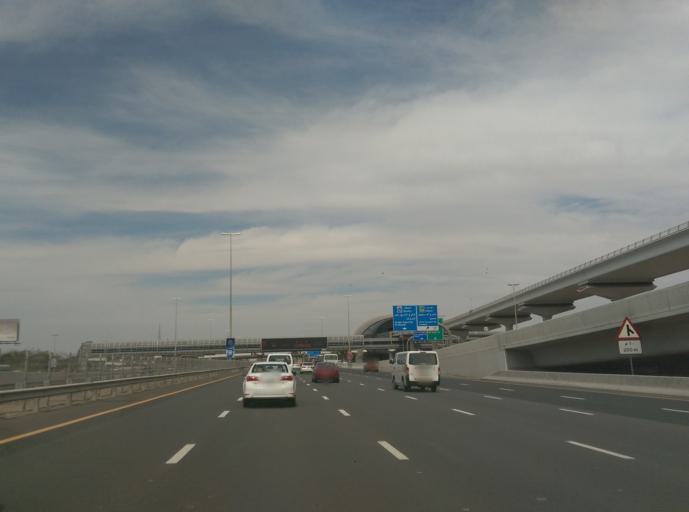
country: AE
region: Dubai
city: Dubai
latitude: 25.1195
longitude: 55.1971
